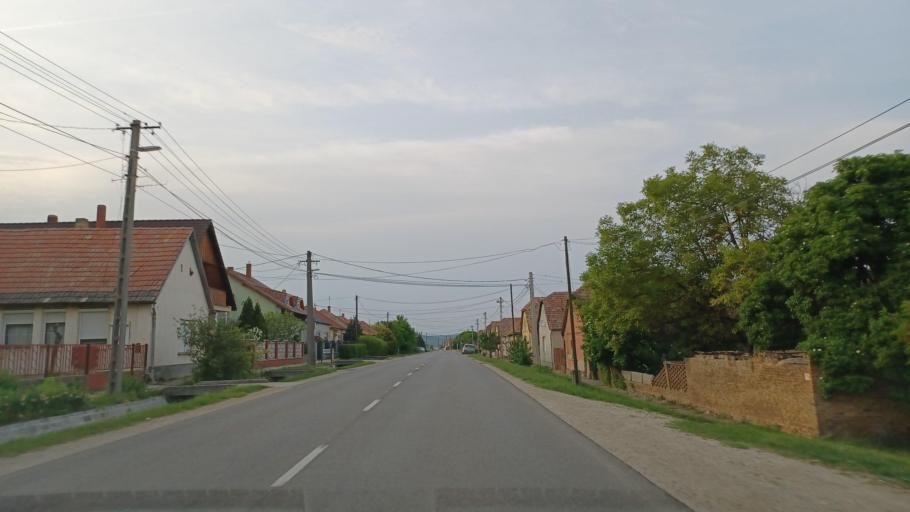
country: HU
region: Tolna
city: Bataszek
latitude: 46.2539
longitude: 18.6853
